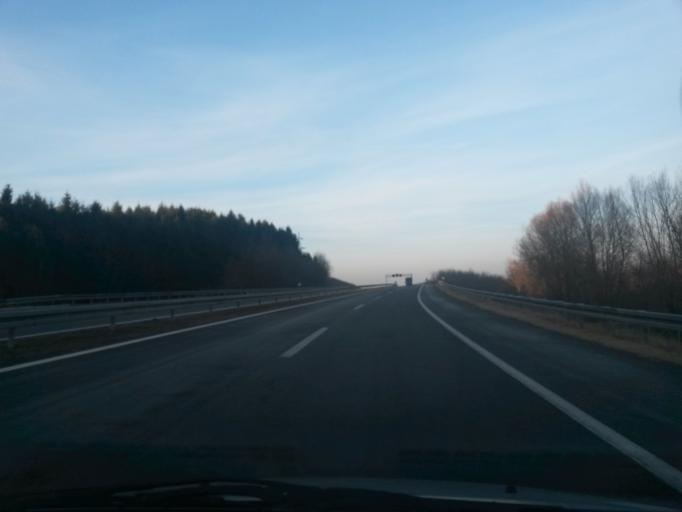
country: HR
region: Varazdinska
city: Jalzabet
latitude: 46.2467
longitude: 16.4008
